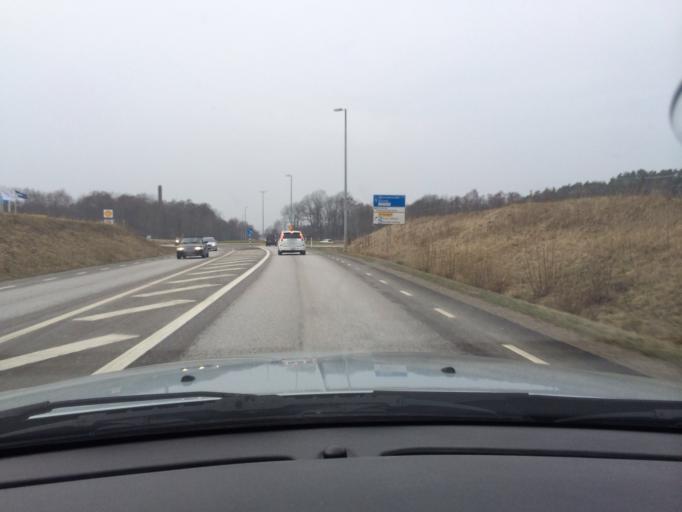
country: SE
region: Vaestra Goetaland
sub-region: Stenungsunds Kommun
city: Stenungsund
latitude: 58.0689
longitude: 11.8579
